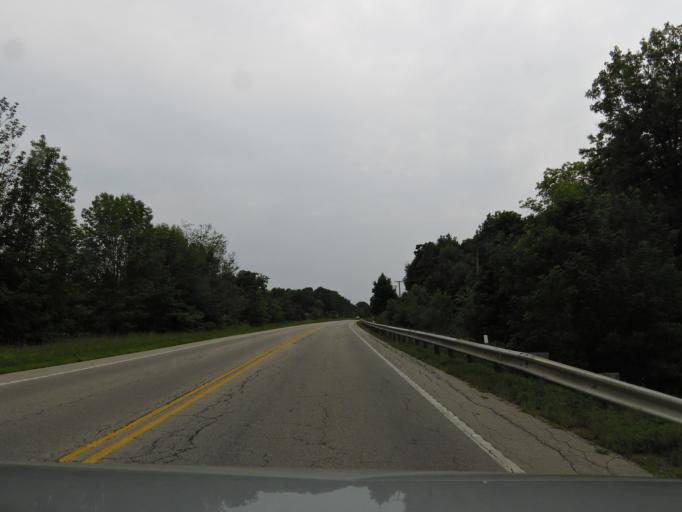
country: US
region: Ohio
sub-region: Clinton County
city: Wilmington
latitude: 39.3799
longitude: -83.8601
